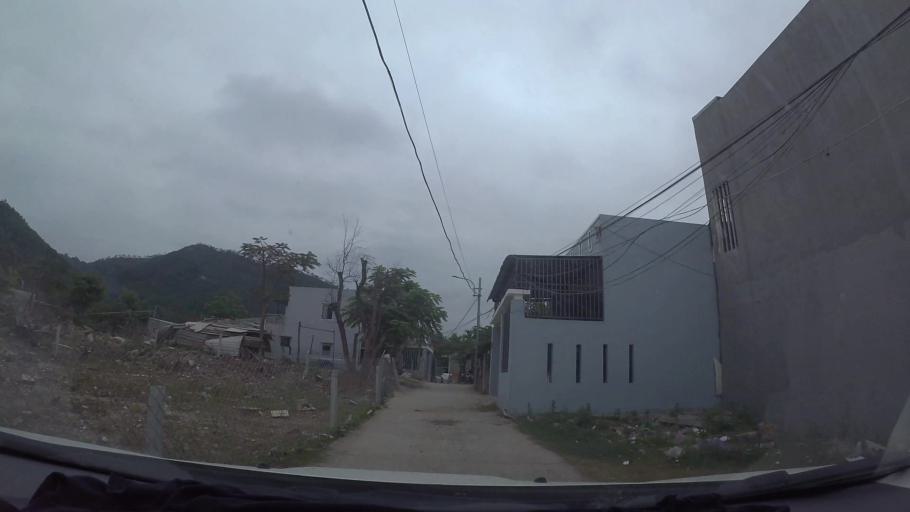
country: VN
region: Da Nang
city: Lien Chieu
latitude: 16.0704
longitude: 108.1394
